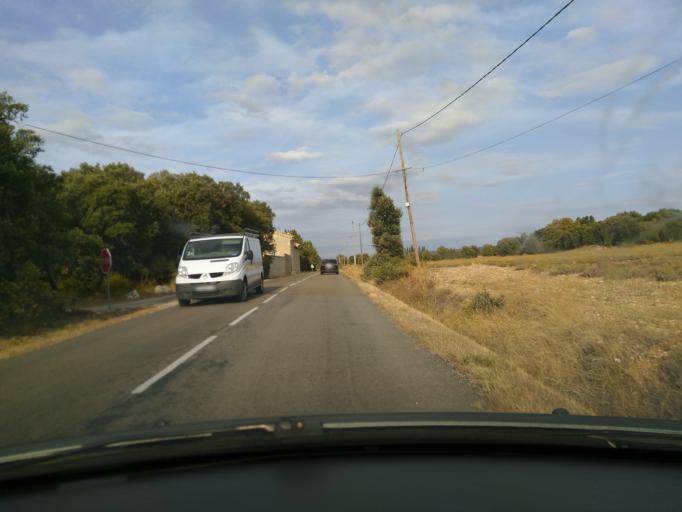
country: FR
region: Rhone-Alpes
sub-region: Departement de la Drome
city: Taulignan
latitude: 44.4423
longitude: 5.0007
